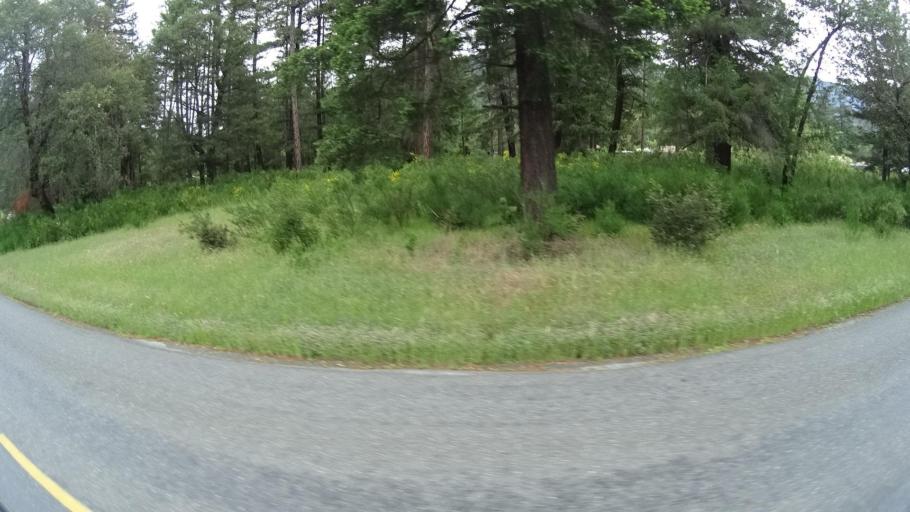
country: US
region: California
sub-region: Humboldt County
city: Willow Creek
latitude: 40.9480
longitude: -123.6304
